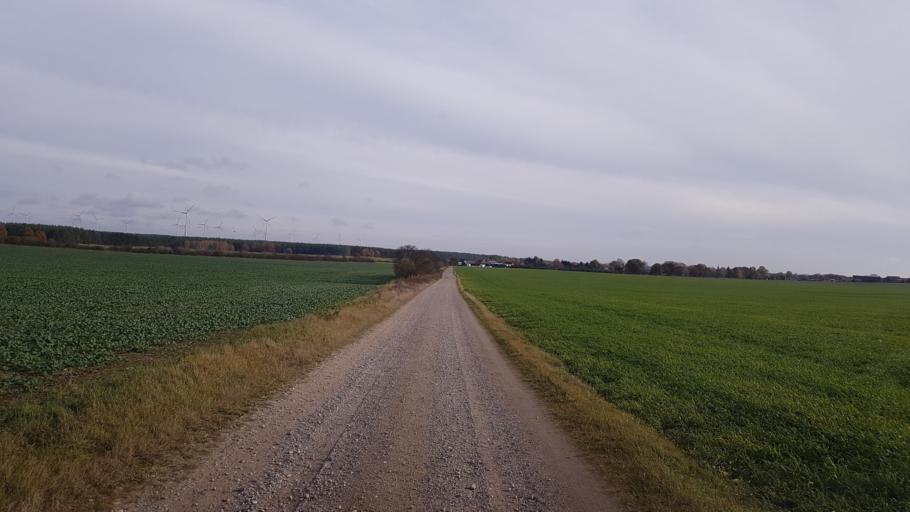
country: DE
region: Brandenburg
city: Niedergorsdorf
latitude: 52.0147
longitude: 12.9077
